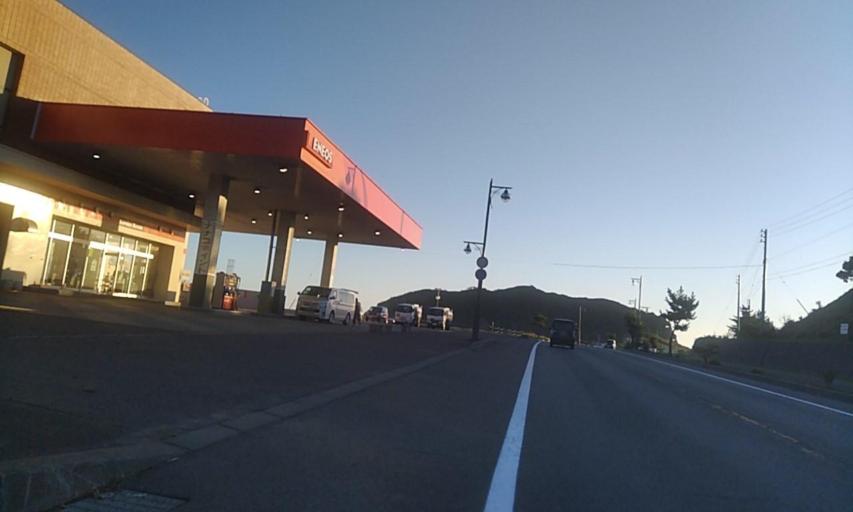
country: JP
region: Hokkaido
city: Shizunai-furukawacho
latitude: 42.1273
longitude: 142.9263
